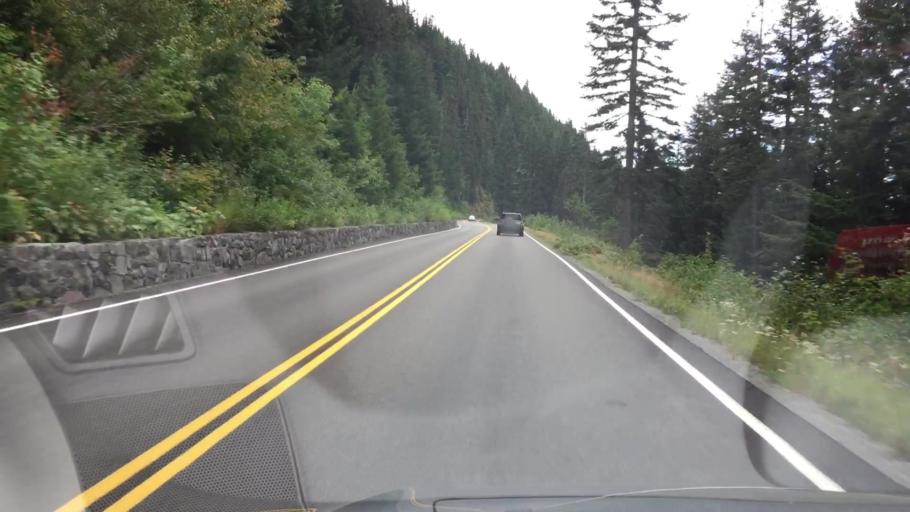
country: US
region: Washington
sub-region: Pierce County
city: Buckley
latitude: 46.7765
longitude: -121.7666
